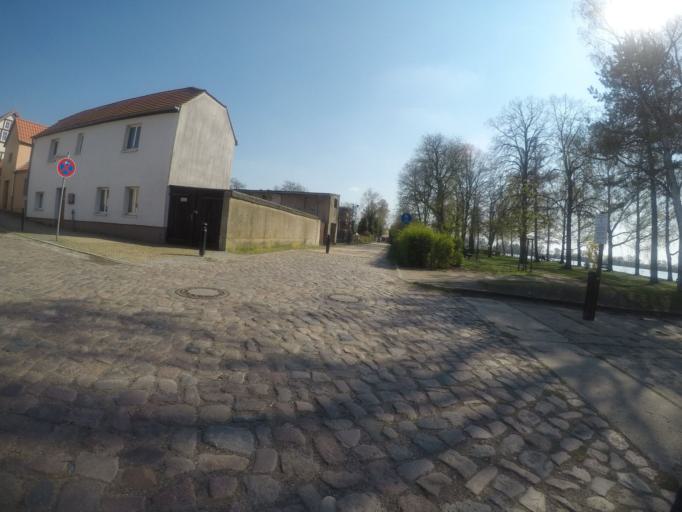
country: DE
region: Brandenburg
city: Ketzin
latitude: 52.4752
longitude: 12.8400
